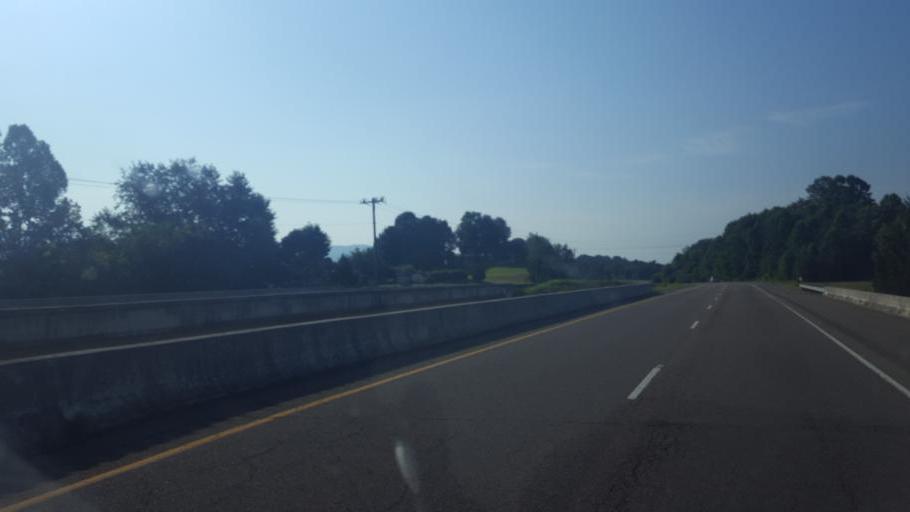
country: US
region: Tennessee
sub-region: Sullivan County
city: Bluff City
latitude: 36.4452
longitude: -82.2740
